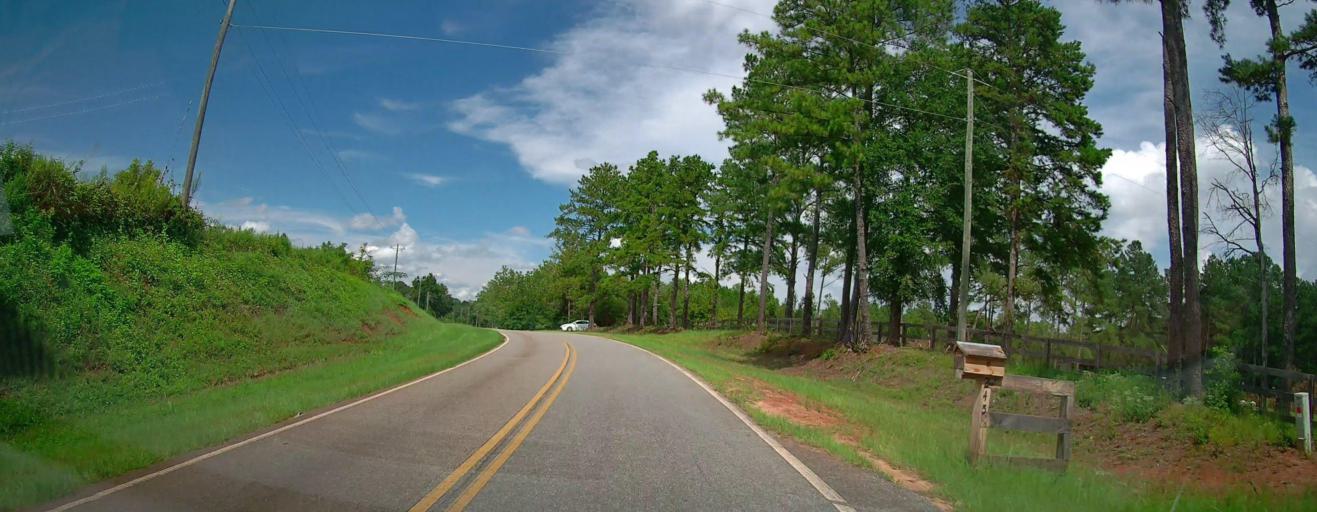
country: US
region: Georgia
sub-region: Houston County
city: Perry
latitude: 32.5145
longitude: -83.7467
